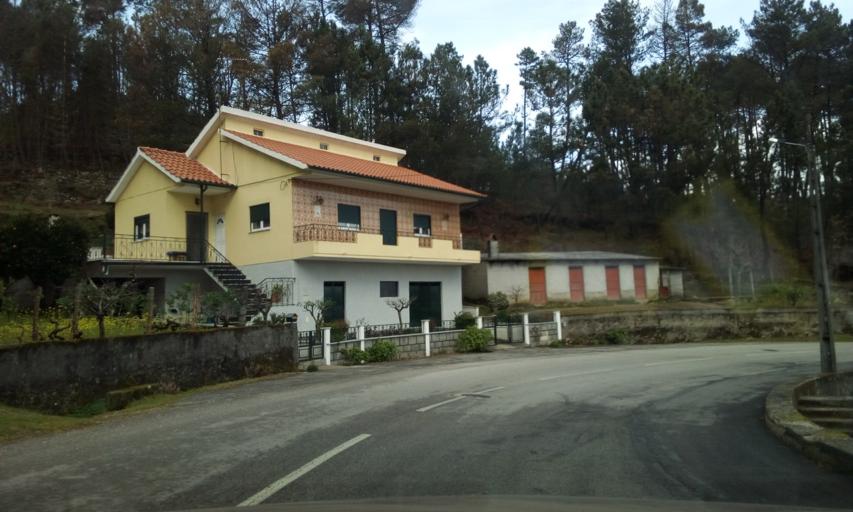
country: PT
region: Guarda
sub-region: Fornos de Algodres
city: Fornos de Algodres
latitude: 40.6642
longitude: -7.6101
